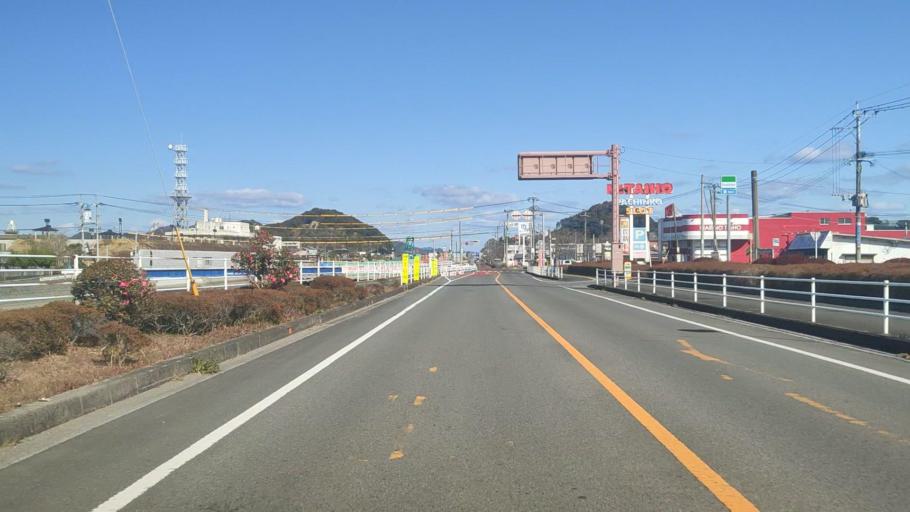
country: JP
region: Oita
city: Saiki
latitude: 32.9512
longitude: 131.9052
